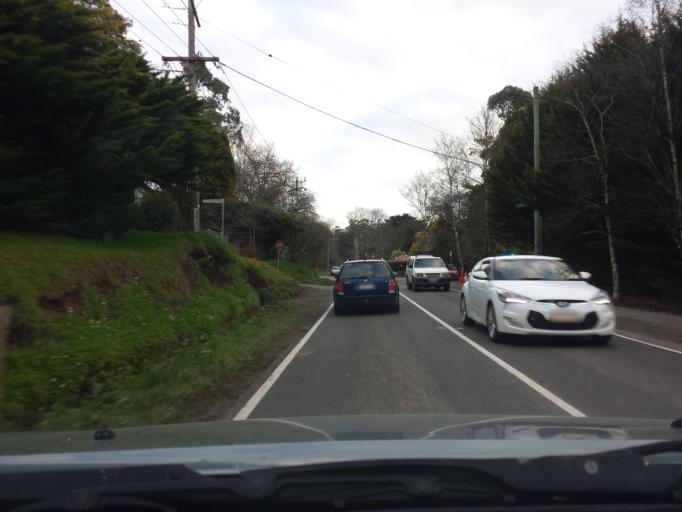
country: AU
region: Victoria
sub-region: Yarra Ranges
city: Kallista
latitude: -37.8816
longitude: 145.3717
